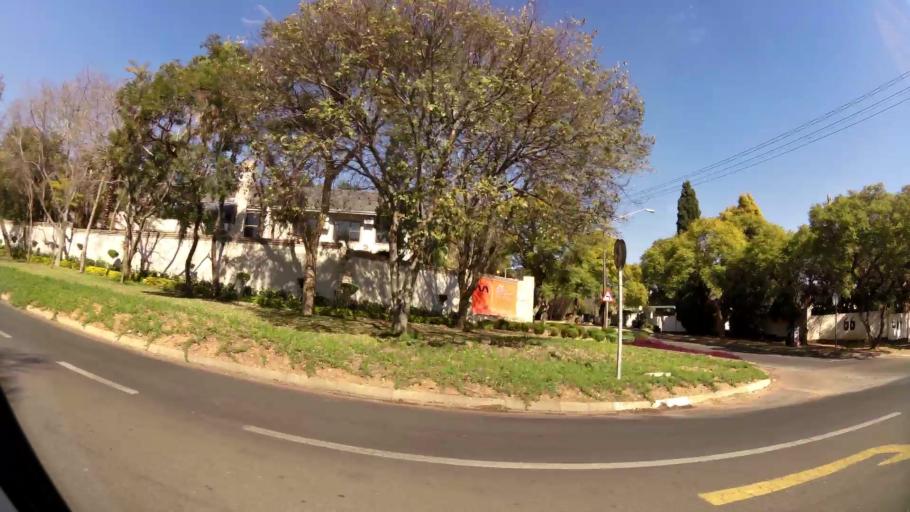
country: ZA
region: Gauteng
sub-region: City of Tshwane Metropolitan Municipality
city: Pretoria
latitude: -25.7849
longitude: 28.2351
